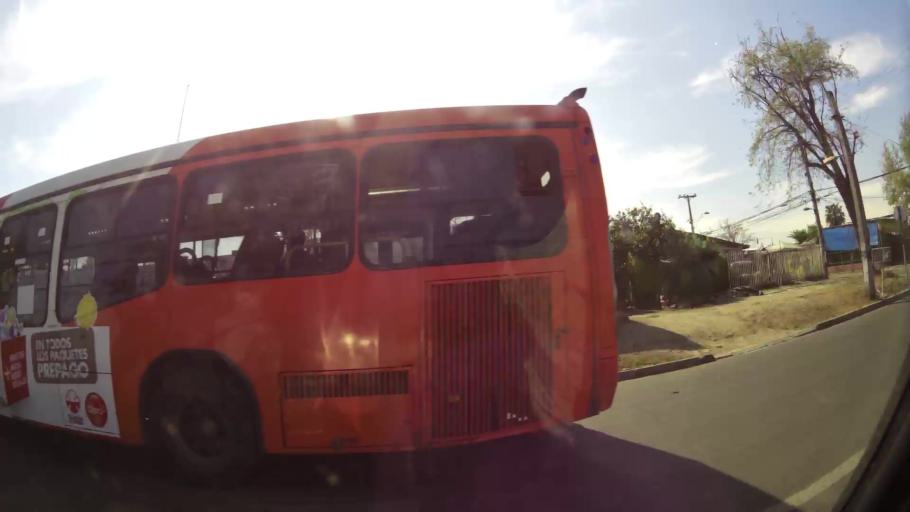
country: CL
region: Santiago Metropolitan
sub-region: Provincia de Santiago
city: Lo Prado
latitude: -33.4810
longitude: -70.7394
